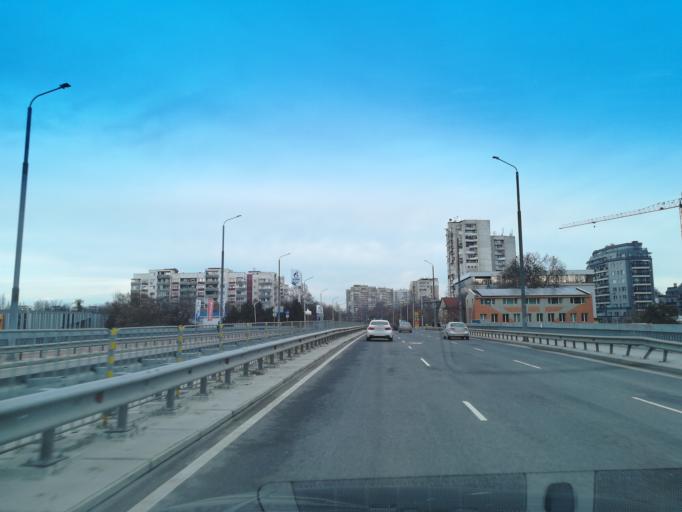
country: BG
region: Plovdiv
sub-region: Obshtina Plovdiv
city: Plovdiv
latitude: 42.1537
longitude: 24.7312
